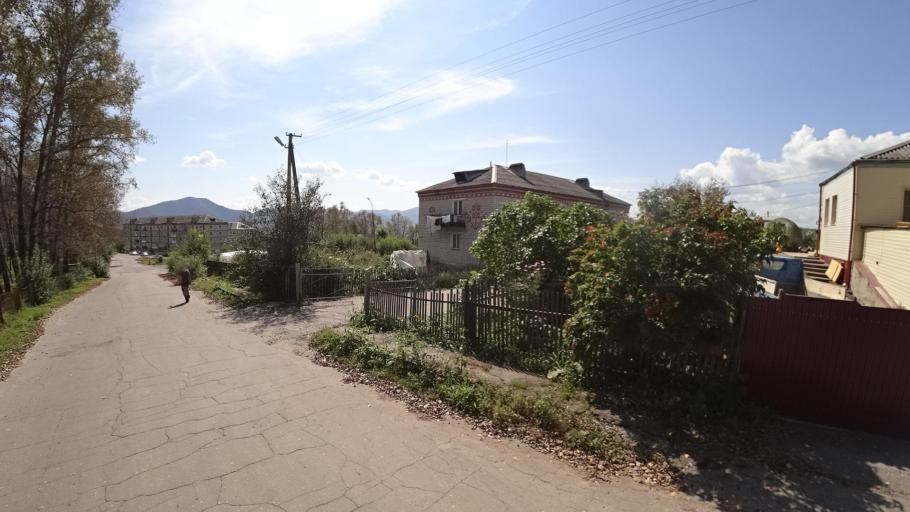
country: RU
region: Jewish Autonomous Oblast
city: Londoko
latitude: 49.0167
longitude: 131.8872
